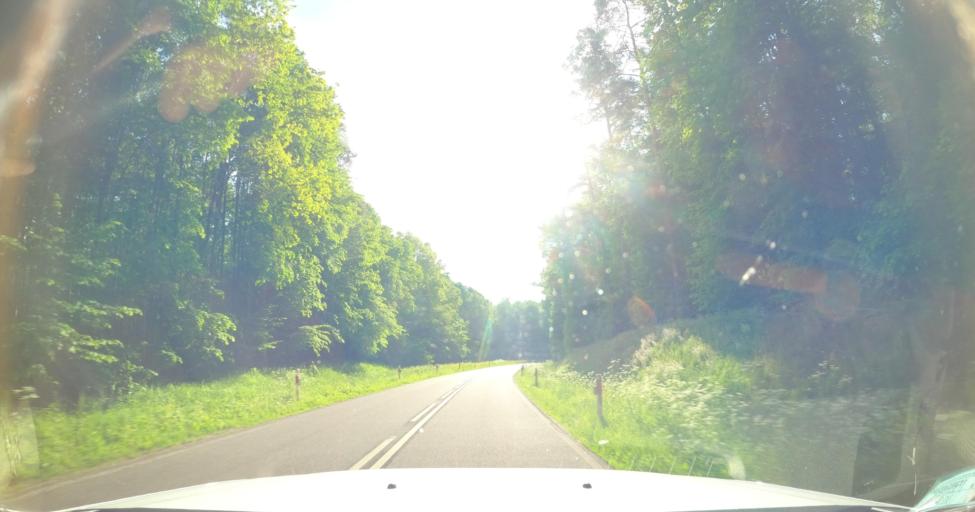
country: PL
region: Warmian-Masurian Voivodeship
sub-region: Powiat elblaski
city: Paslek
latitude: 54.0790
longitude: 19.7270
